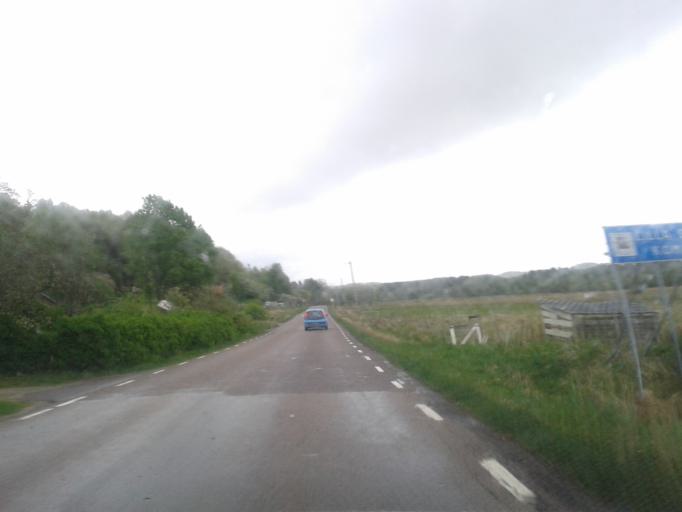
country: SE
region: Vaestra Goetaland
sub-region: Lilla Edets Kommun
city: Lodose
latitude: 58.0115
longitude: 12.1276
